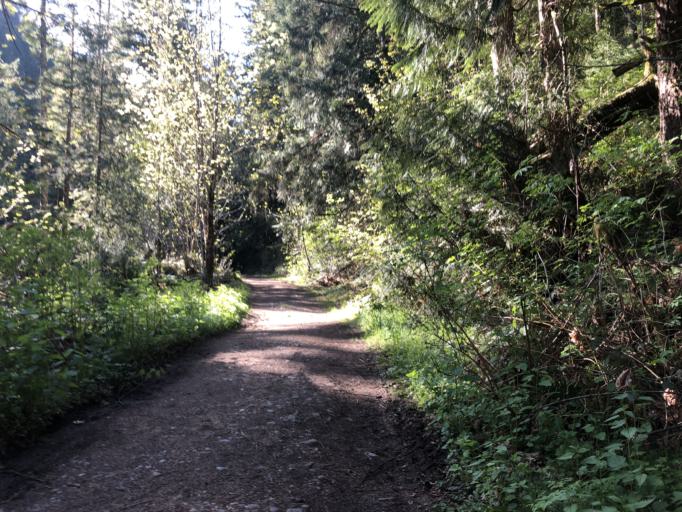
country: US
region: Washington
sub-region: Pierce County
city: Buckley
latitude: 47.0406
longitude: -122.0390
